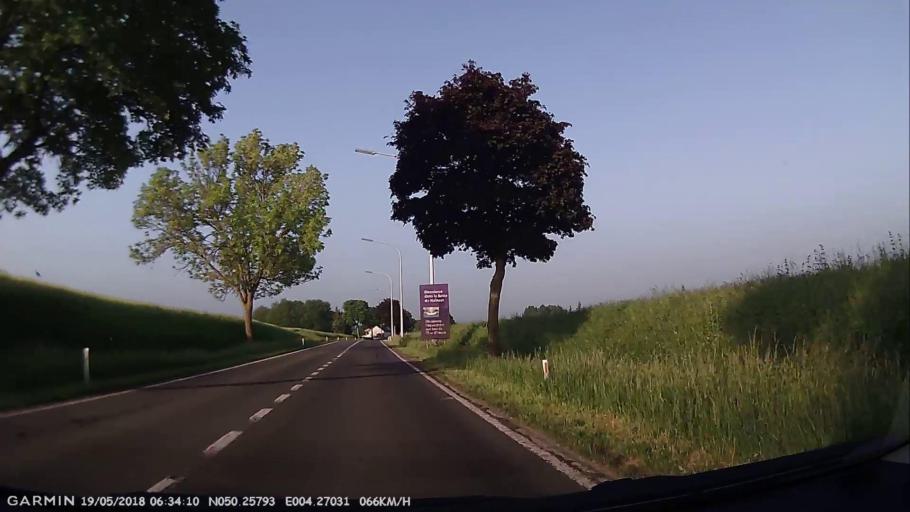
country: BE
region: Wallonia
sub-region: Province du Hainaut
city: Beaumont
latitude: 50.2579
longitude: 4.2703
